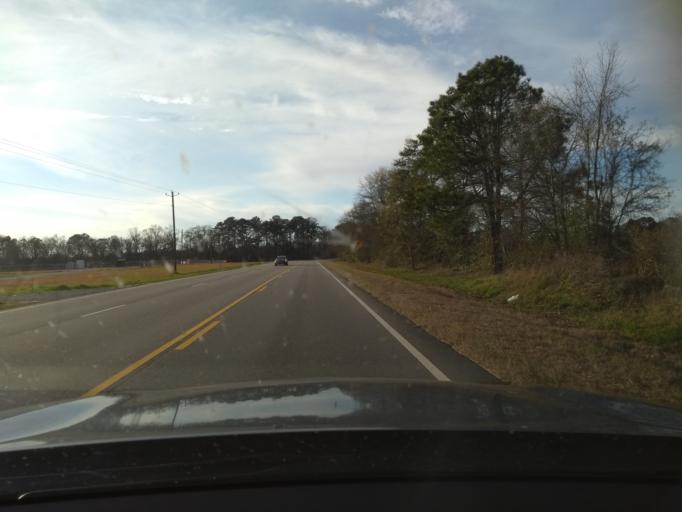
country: US
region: Georgia
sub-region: Bulloch County
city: Brooklet
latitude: 32.2935
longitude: -81.7676
